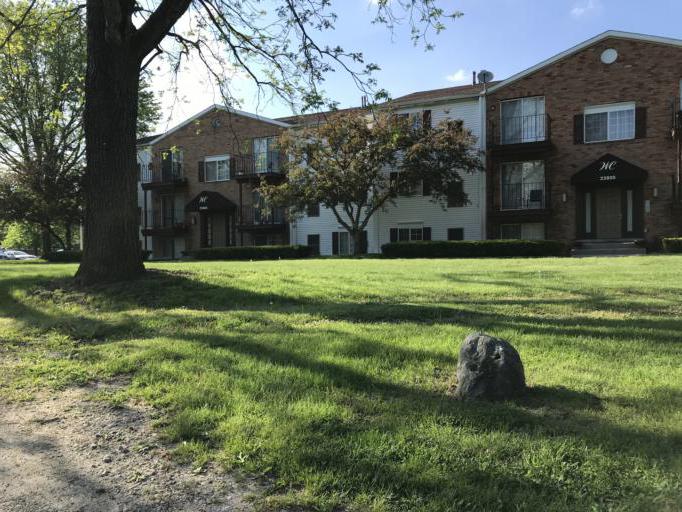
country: US
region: Michigan
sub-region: Oakland County
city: Farmington
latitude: 42.4671
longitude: -83.3358
